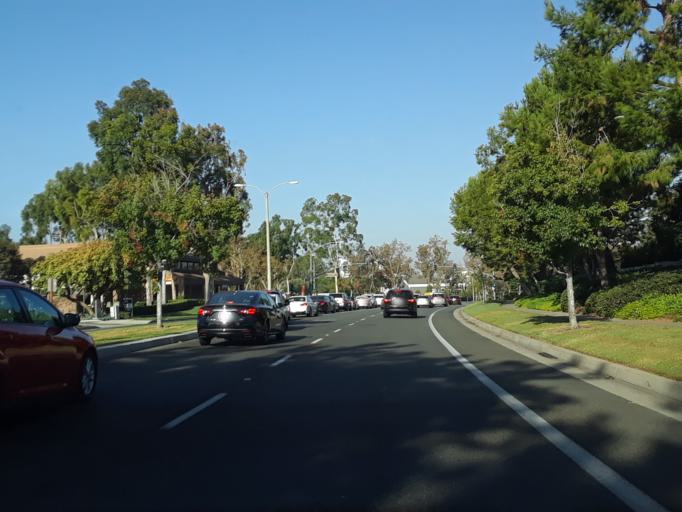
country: US
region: California
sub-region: Orange County
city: Irvine
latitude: 33.6765
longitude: -117.7958
